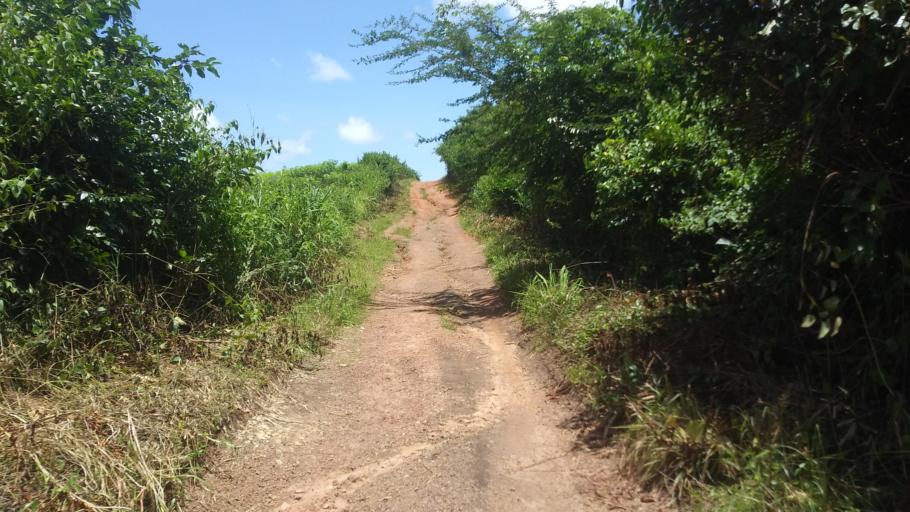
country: SL
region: Northern Province
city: Makeni
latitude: 8.8961
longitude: -12.0004
